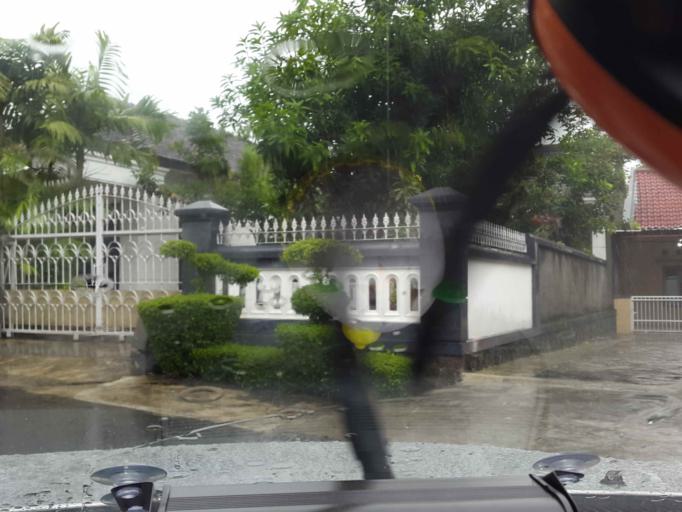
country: ID
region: Central Java
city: Jaten
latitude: -7.6025
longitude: 110.9734
